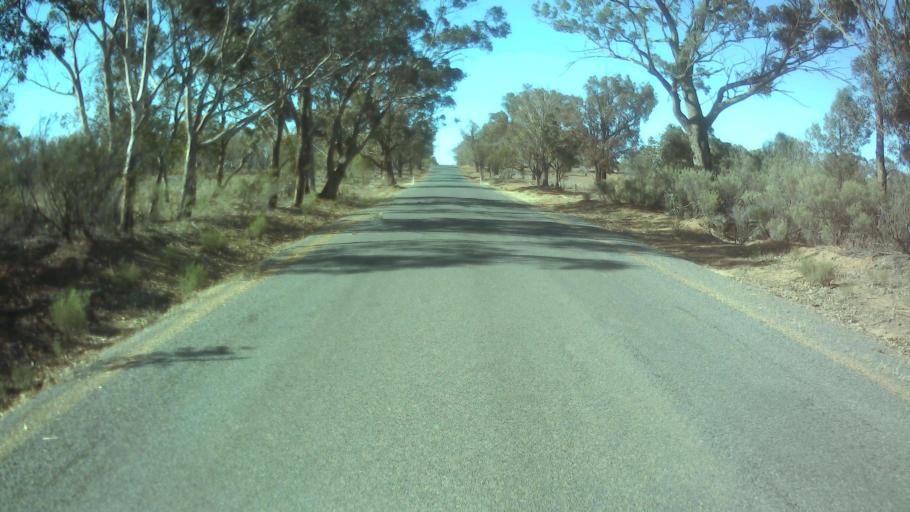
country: AU
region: New South Wales
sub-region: Forbes
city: Forbes
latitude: -33.7076
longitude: 147.8053
